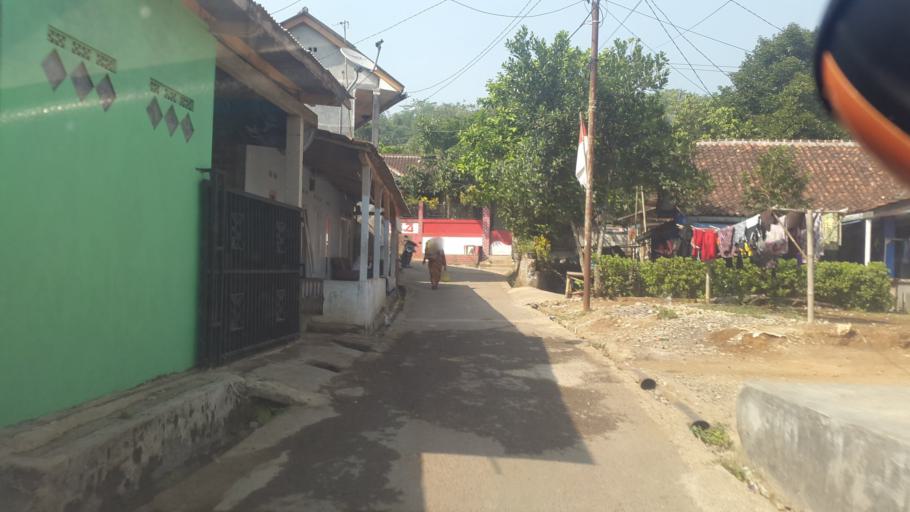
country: ID
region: West Java
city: Gunungkalong
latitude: -6.8967
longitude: 106.7983
